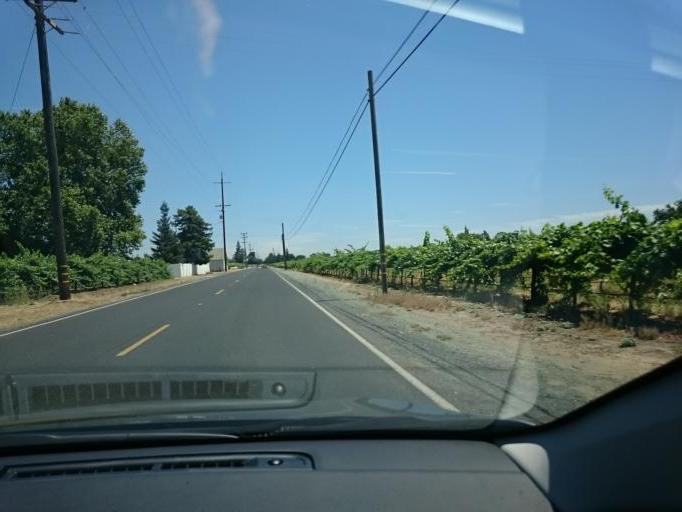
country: US
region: California
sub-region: San Joaquin County
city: Collierville
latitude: 38.1890
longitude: -121.2383
